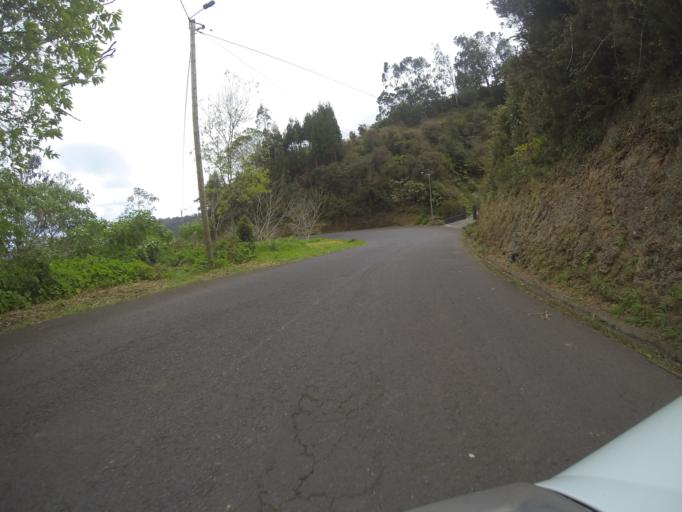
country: PT
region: Madeira
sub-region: Santa Cruz
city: Santa Cruz
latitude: 32.7426
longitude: -16.8257
